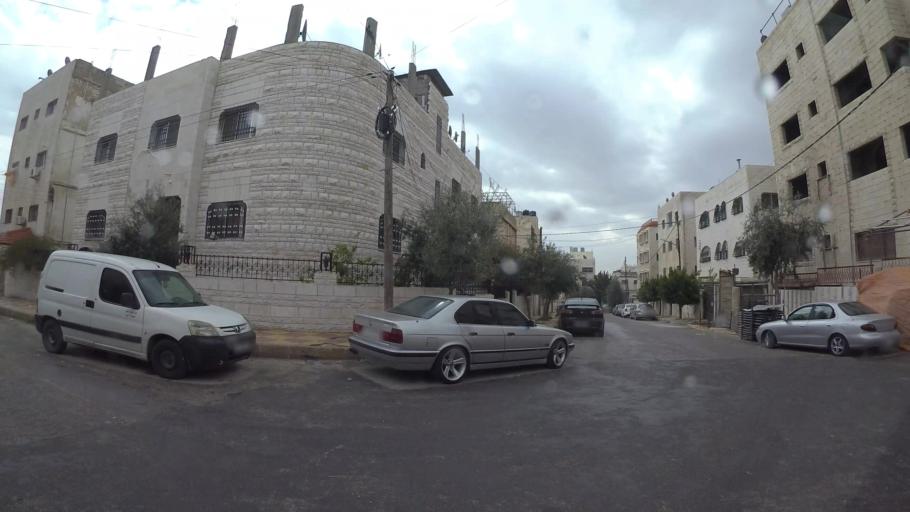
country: JO
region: Amman
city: Amman
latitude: 31.9837
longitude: 35.9262
